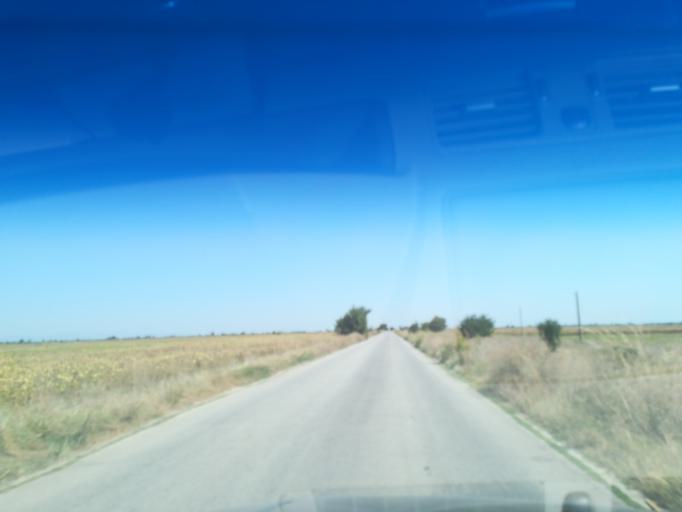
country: BG
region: Plovdiv
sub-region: Obshtina Suedinenie
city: Suedinenie
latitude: 42.2517
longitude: 24.4551
